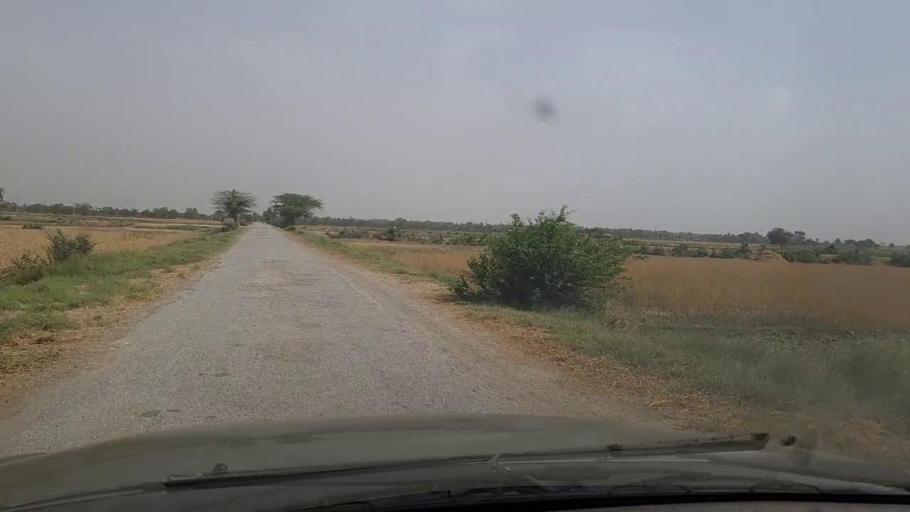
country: PK
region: Sindh
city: Lakhi
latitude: 27.8495
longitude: 68.7532
